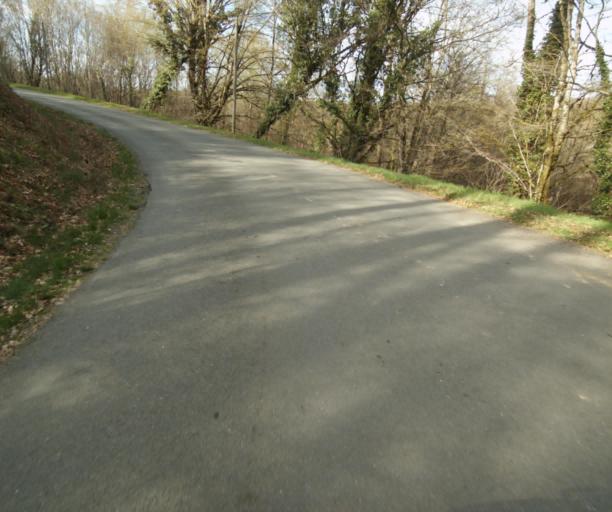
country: FR
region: Limousin
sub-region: Departement de la Correze
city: Naves
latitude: 45.3143
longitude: 1.7296
